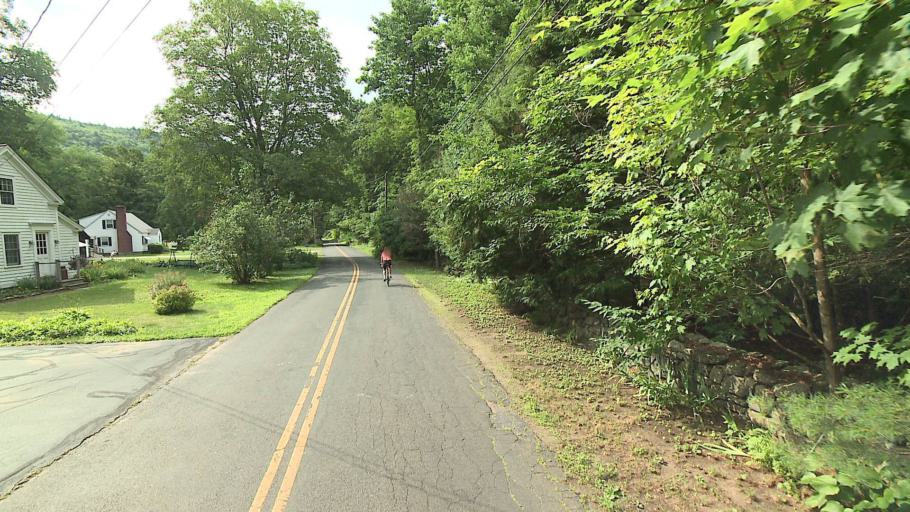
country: US
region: Connecticut
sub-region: Litchfield County
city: Winsted
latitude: 41.9587
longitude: -73.0162
